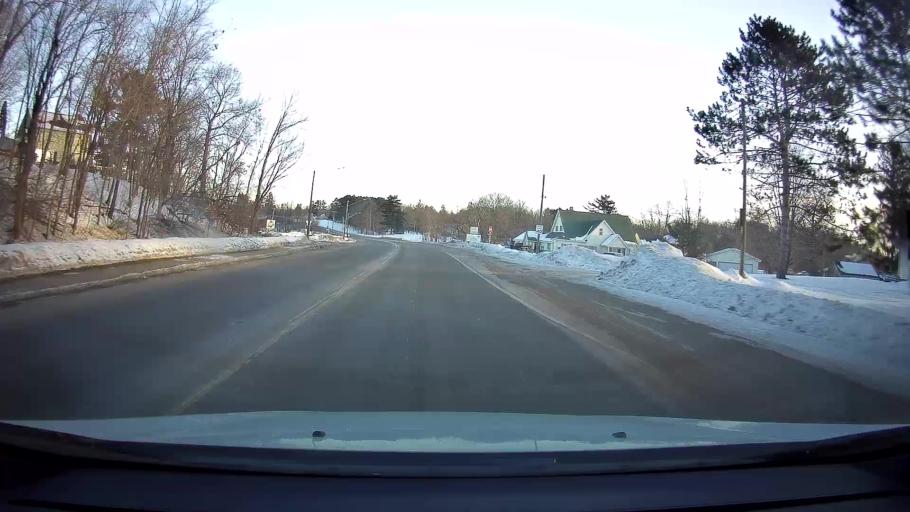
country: US
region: Wisconsin
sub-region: Barron County
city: Cumberland
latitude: 45.5421
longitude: -92.0192
